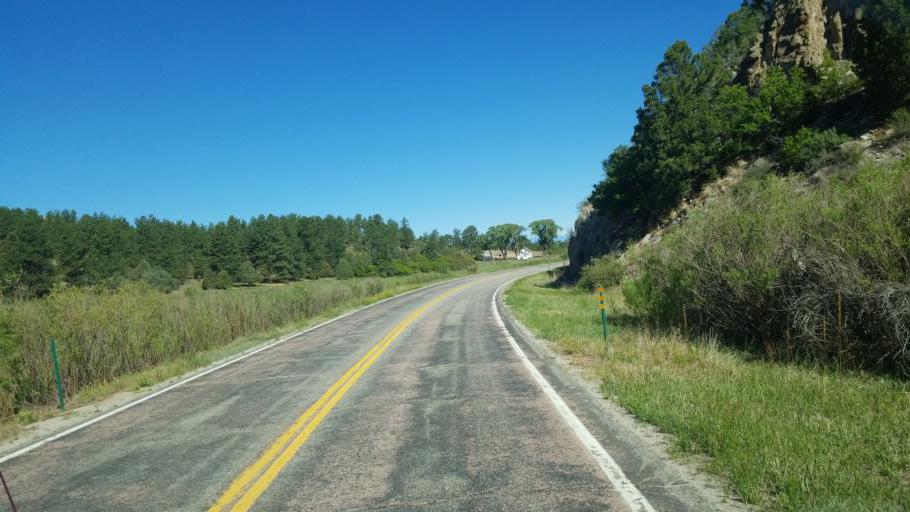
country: US
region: Colorado
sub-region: Custer County
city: Westcliffe
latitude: 38.2382
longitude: -105.5636
